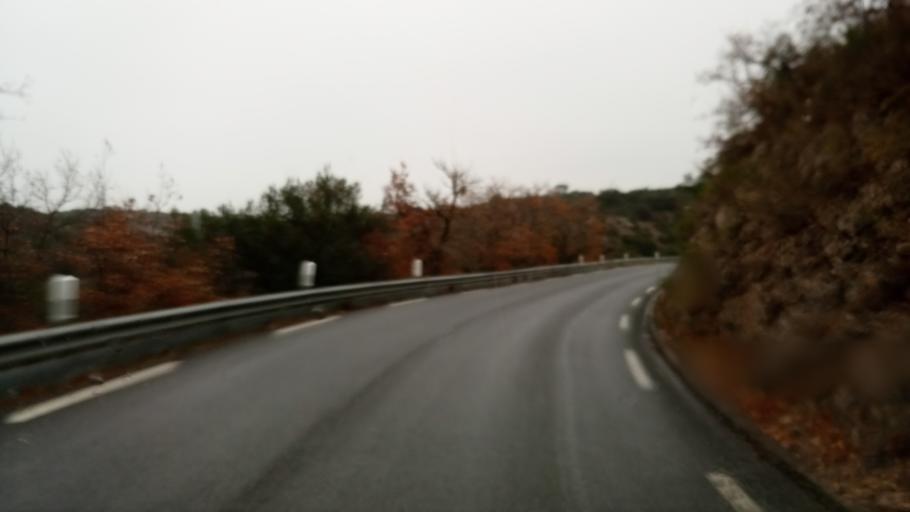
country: FR
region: Provence-Alpes-Cote d'Azur
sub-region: Departement du Var
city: Saint-Julien
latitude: 43.7016
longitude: 5.8827
